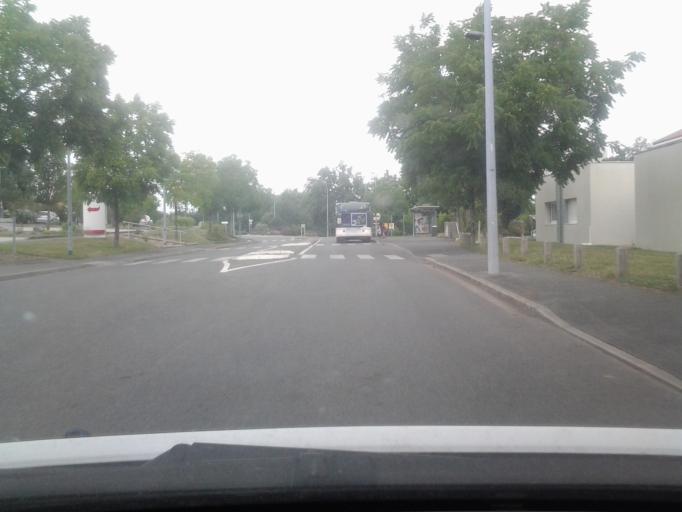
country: FR
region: Pays de la Loire
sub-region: Departement de la Vendee
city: La Roche-sur-Yon
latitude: 46.6566
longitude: -1.4236
